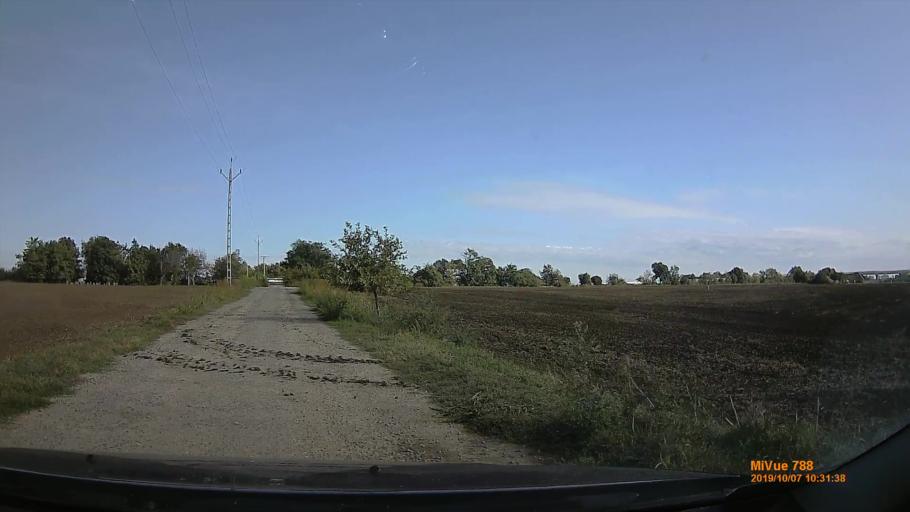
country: HU
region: Bekes
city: Kondoros
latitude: 46.7464
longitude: 20.8448
